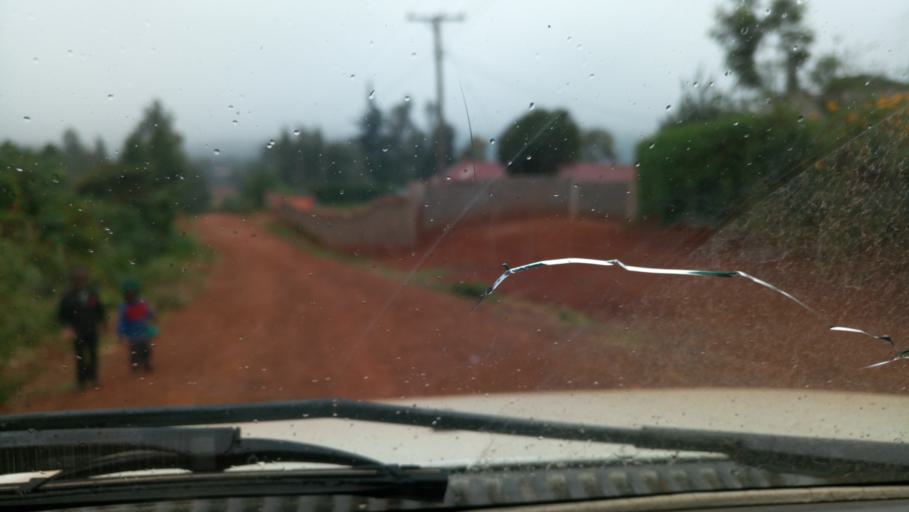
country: KE
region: Murang'a District
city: Kangema
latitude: -0.6501
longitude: 36.9738
